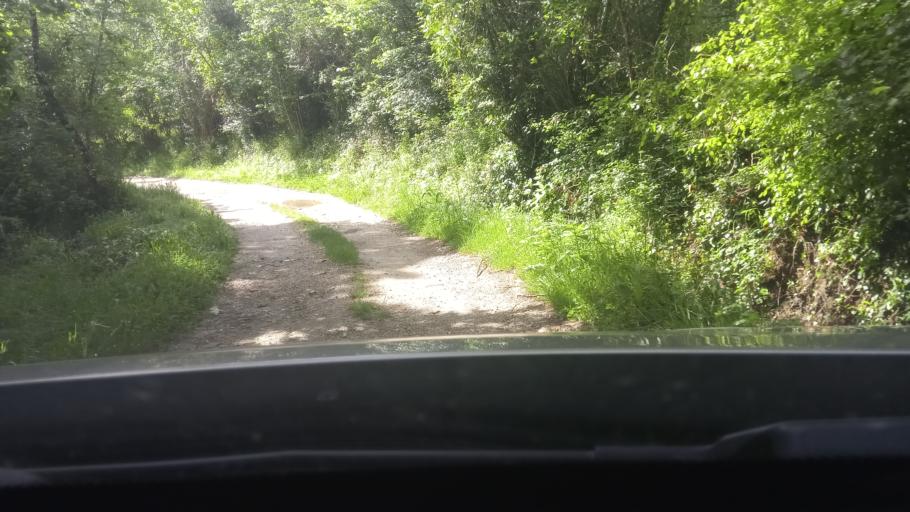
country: IT
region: Latium
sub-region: Provincia di Latina
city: Minturno
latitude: 41.2811
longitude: 13.7633
